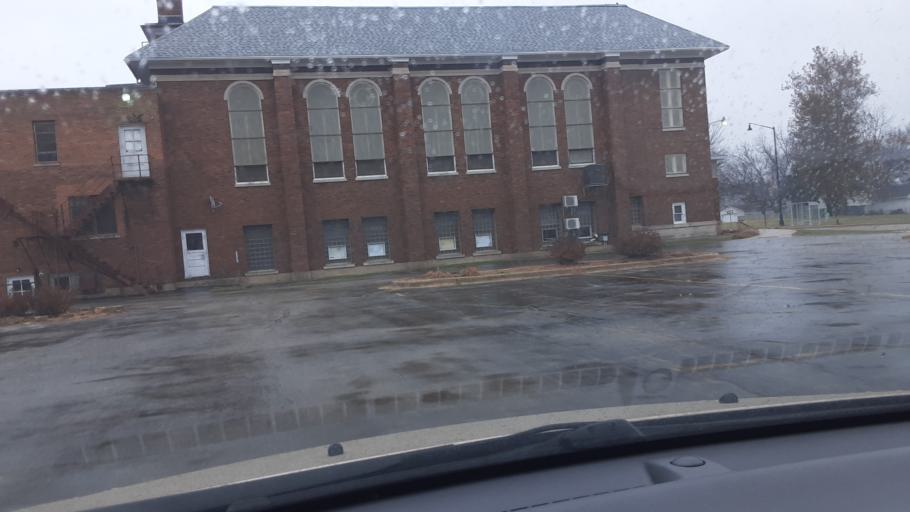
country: US
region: Illinois
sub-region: Winnebago County
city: Rockford
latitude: 42.2763
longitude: -89.1118
